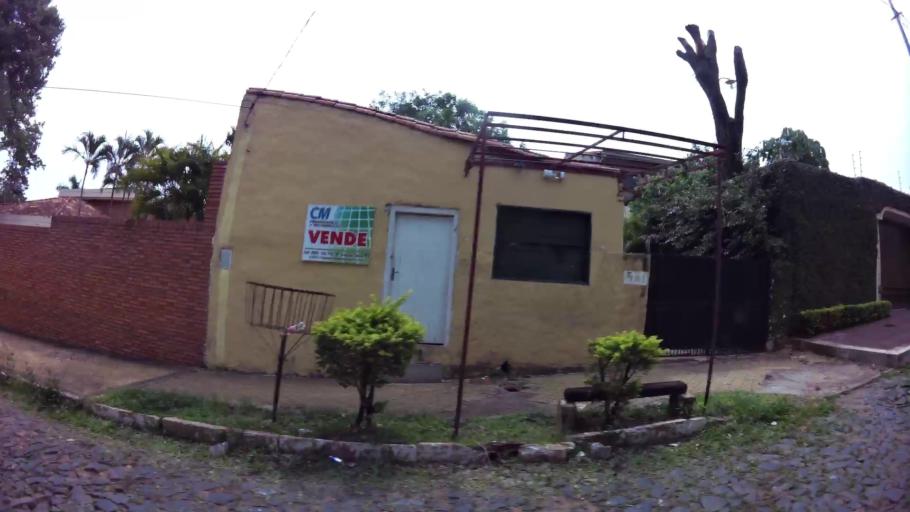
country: PY
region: Asuncion
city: Asuncion
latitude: -25.2907
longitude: -57.5822
